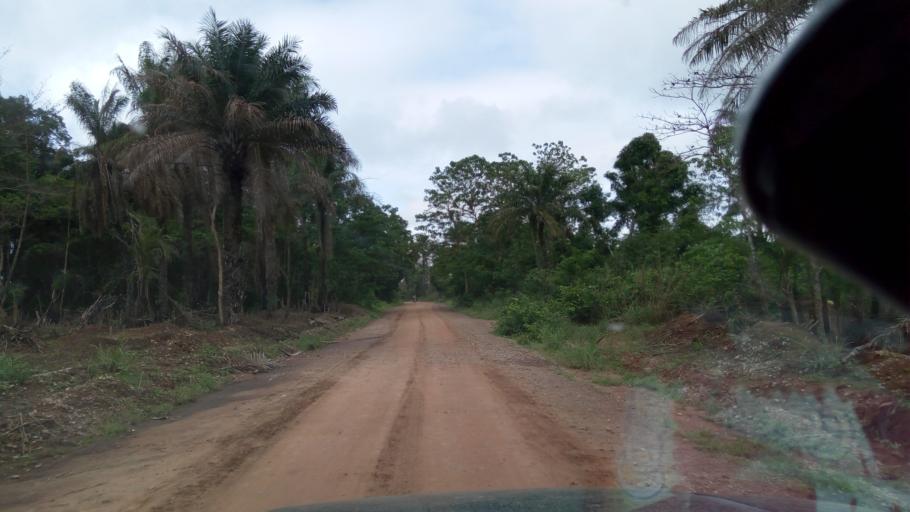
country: SL
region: Northern Province
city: Pepel
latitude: 8.6791
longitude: -13.0002
